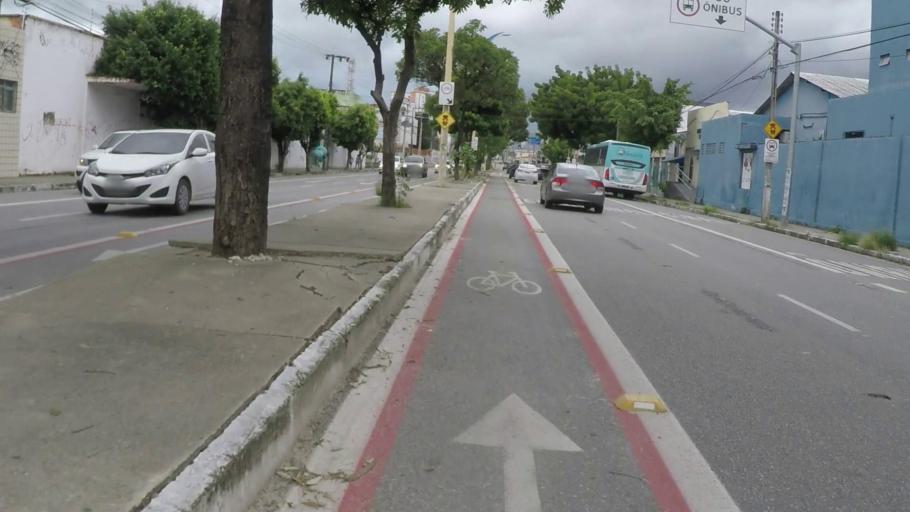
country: BR
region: Ceara
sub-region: Fortaleza
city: Fortaleza
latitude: -3.7343
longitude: -38.5387
